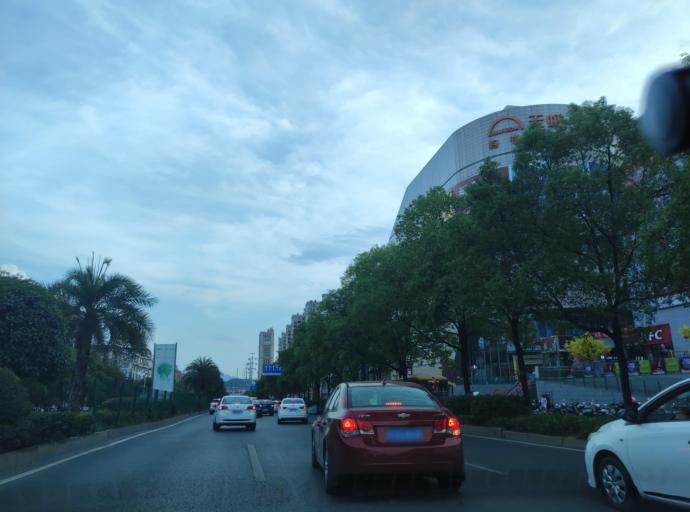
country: CN
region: Jiangxi Sheng
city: Pingxiang
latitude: 27.6358
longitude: 113.8697
